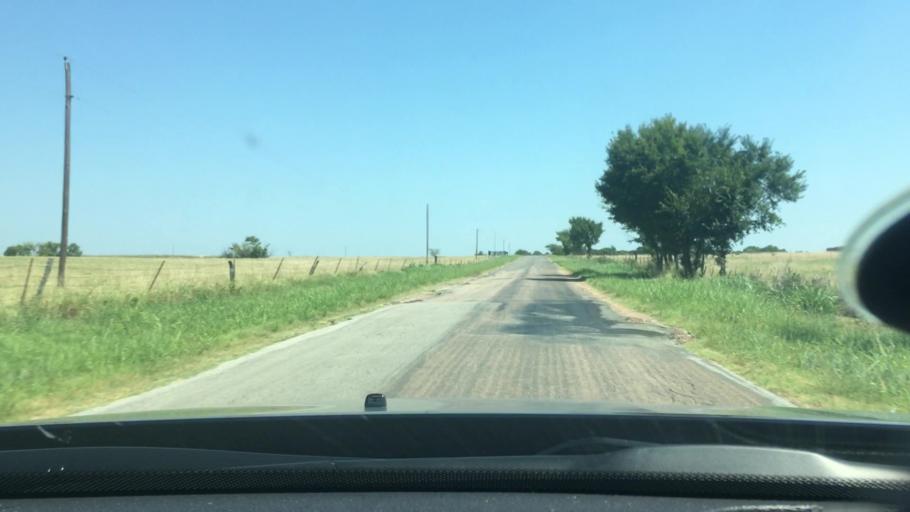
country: US
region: Oklahoma
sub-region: Johnston County
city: Tishomingo
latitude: 34.3131
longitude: -96.6360
